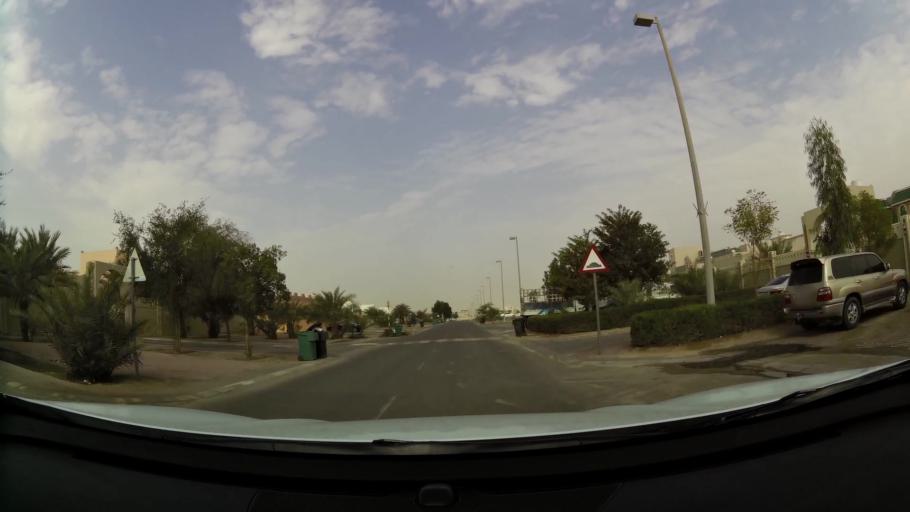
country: AE
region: Abu Dhabi
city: Abu Dhabi
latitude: 24.2854
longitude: 54.6580
